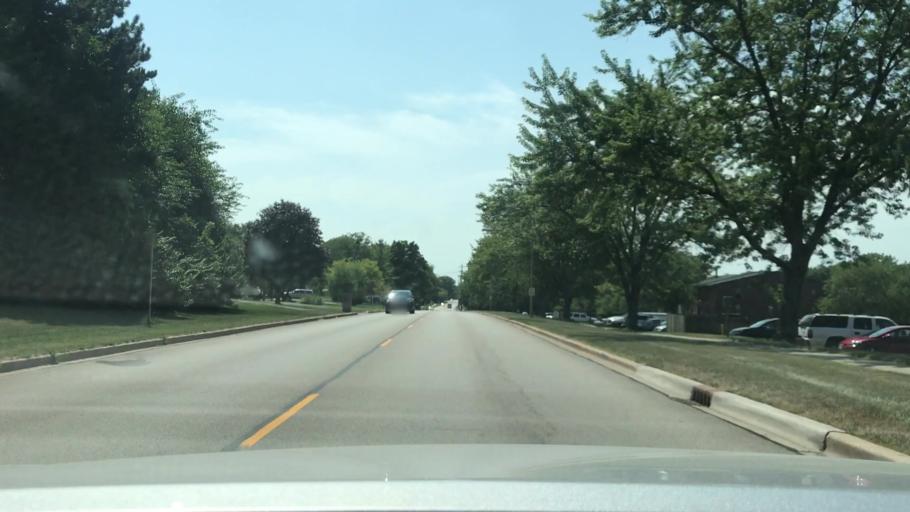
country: US
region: Illinois
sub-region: Kane County
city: Batavia
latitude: 41.8534
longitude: -88.2811
